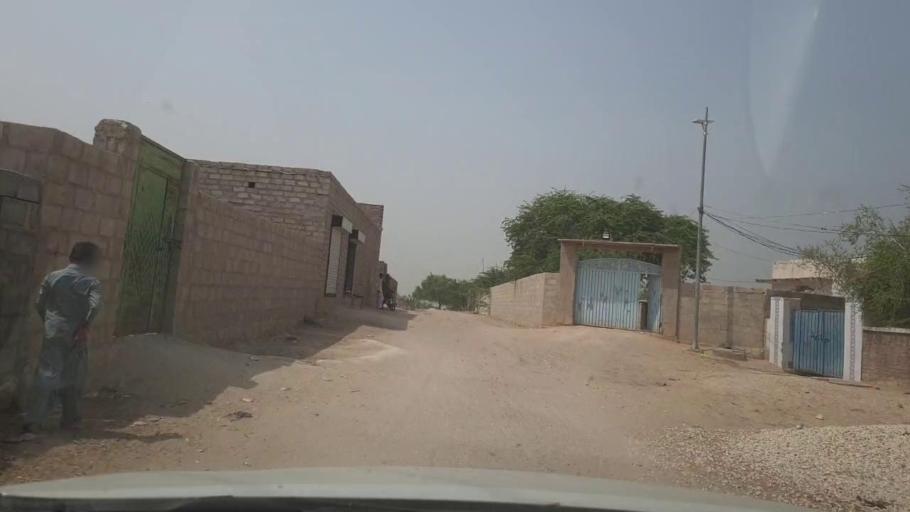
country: PK
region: Sindh
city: Kot Diji
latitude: 27.3371
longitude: 68.7126
